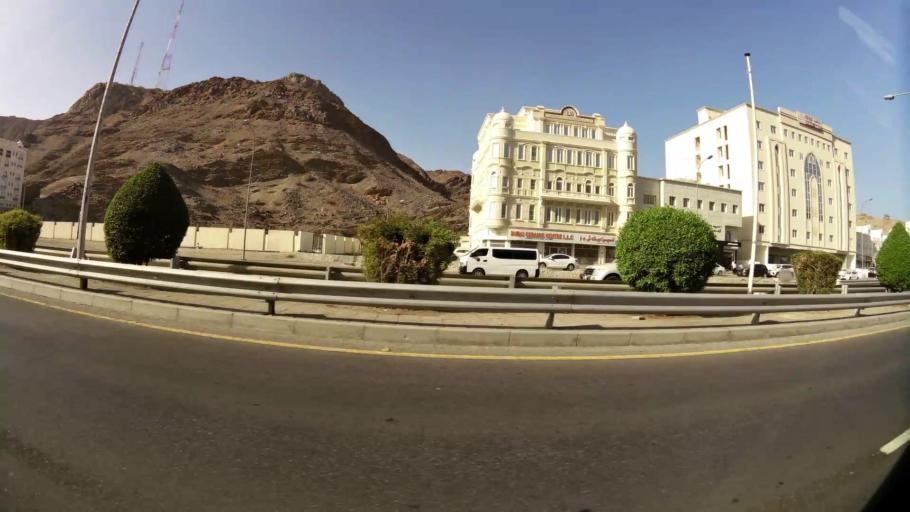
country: OM
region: Muhafazat Masqat
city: Muscat
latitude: 23.5873
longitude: 58.5359
